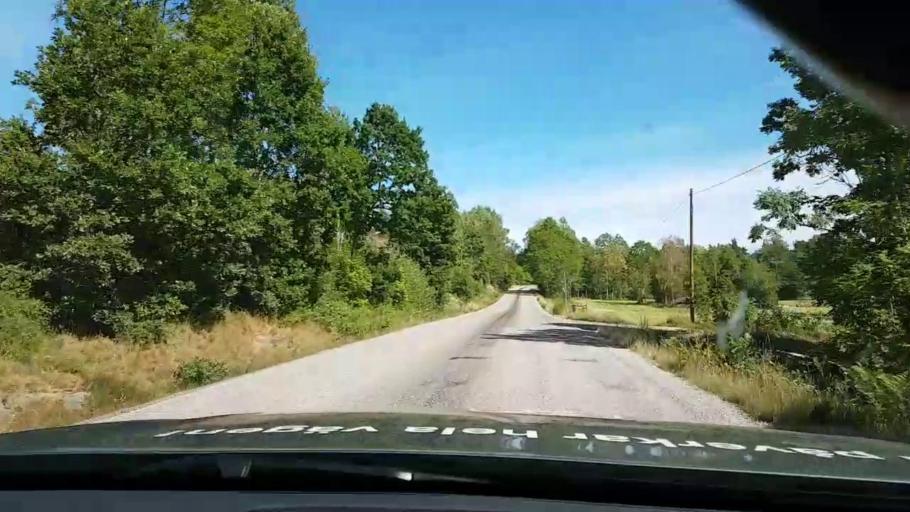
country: SE
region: Kalmar
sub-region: Vasterviks Kommun
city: Vaestervik
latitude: 57.9087
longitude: 16.6573
